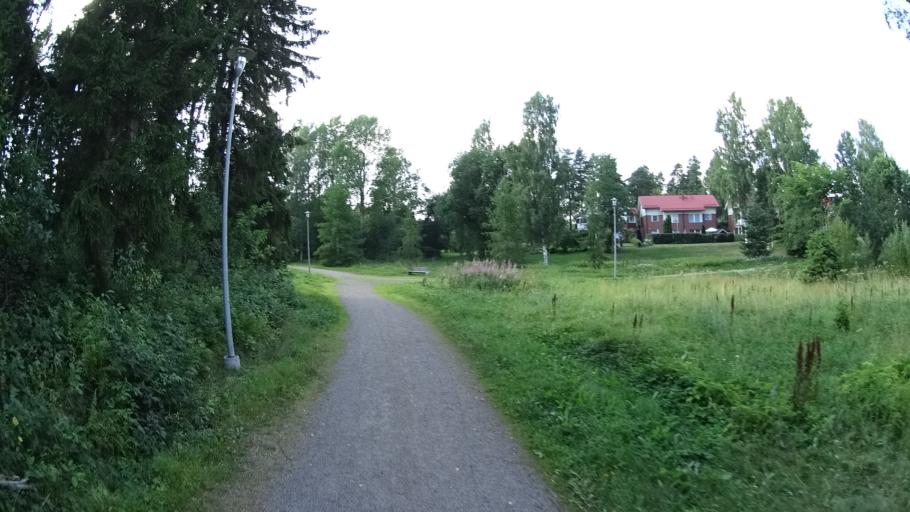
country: FI
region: Uusimaa
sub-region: Porvoo
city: Porvoo
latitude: 60.4074
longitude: 25.6619
